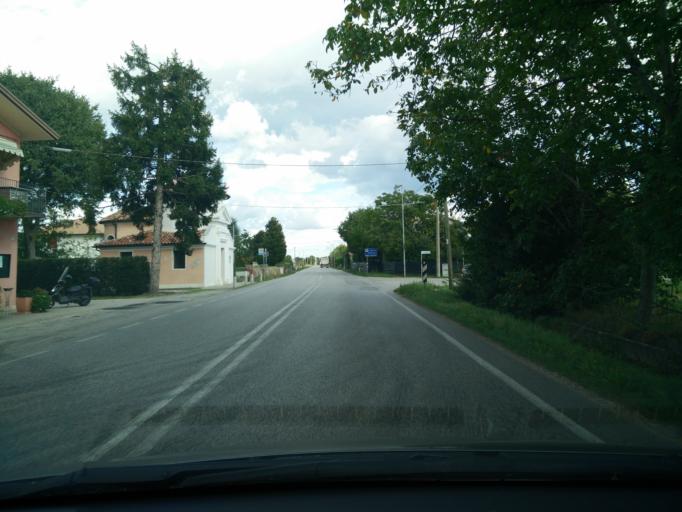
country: IT
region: Veneto
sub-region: Provincia di Treviso
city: Pezzan
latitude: 45.7095
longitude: 12.0762
